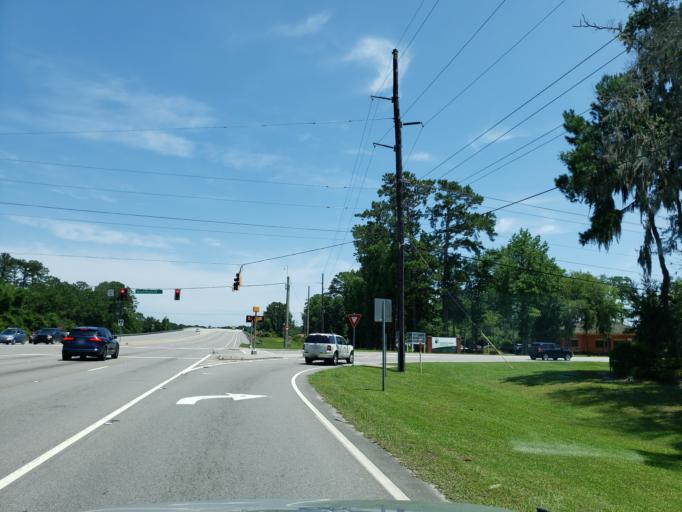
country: US
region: Georgia
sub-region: Chatham County
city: Whitemarsh Island
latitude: 32.0373
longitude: -80.9911
